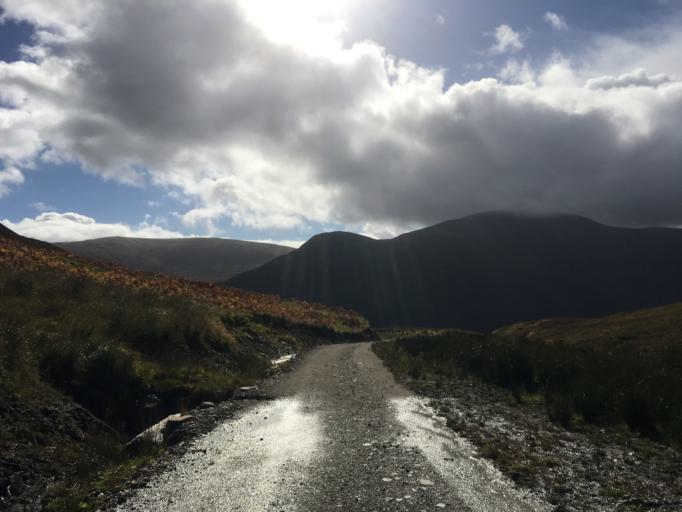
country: GB
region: Scotland
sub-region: Highland
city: Spean Bridge
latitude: 57.3490
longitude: -4.9828
